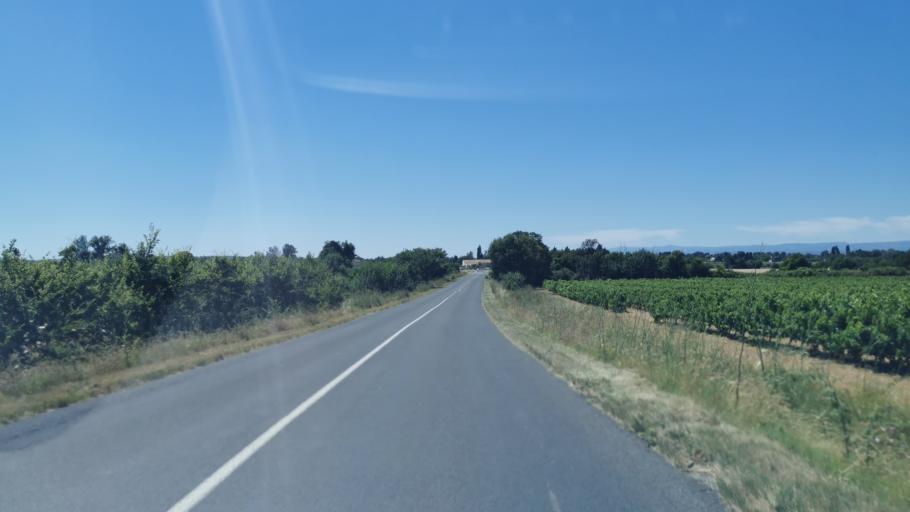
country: FR
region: Languedoc-Roussillon
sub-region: Departement de l'Aude
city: Coursan
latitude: 43.2328
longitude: 3.0813
